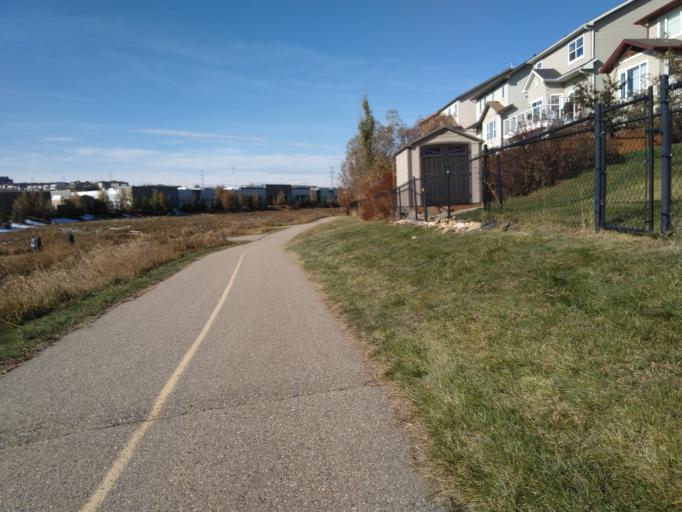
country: CA
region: Alberta
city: Calgary
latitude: 51.1633
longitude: -114.1232
